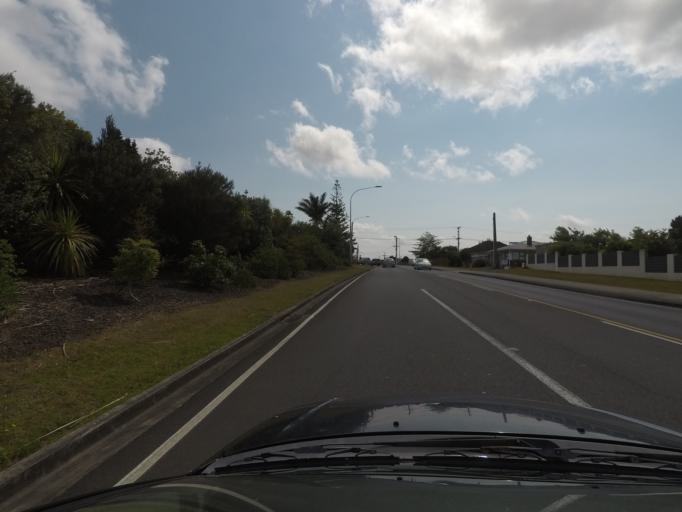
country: NZ
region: Northland
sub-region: Whangarei
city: Whangarei
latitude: -35.6885
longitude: 174.3228
